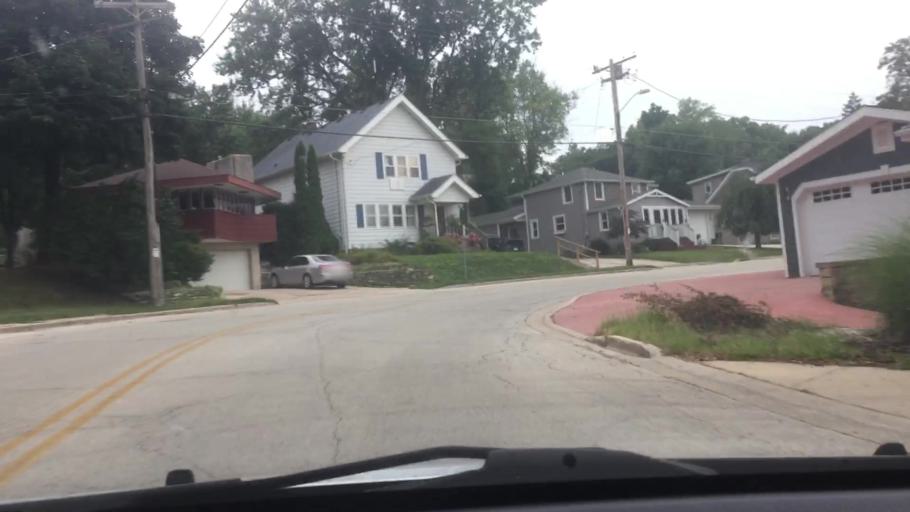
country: US
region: Wisconsin
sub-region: Waukesha County
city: Pewaukee
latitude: 43.0801
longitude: -88.2658
